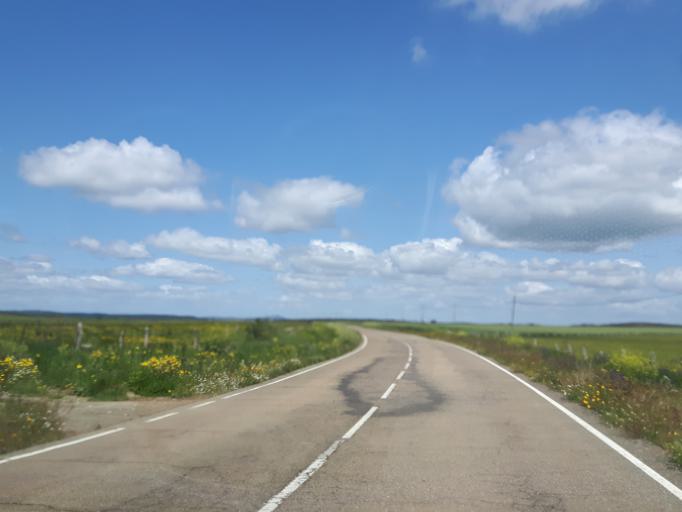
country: ES
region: Castille and Leon
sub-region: Provincia de Salamanca
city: Villar de la Yegua
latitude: 40.7288
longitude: -6.7132
